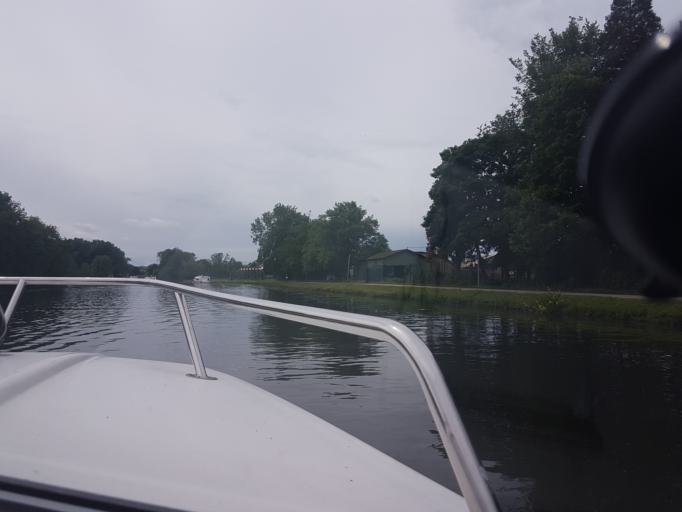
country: FR
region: Bourgogne
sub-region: Departement de l'Yonne
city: Auxerre
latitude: 47.7878
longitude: 3.5903
